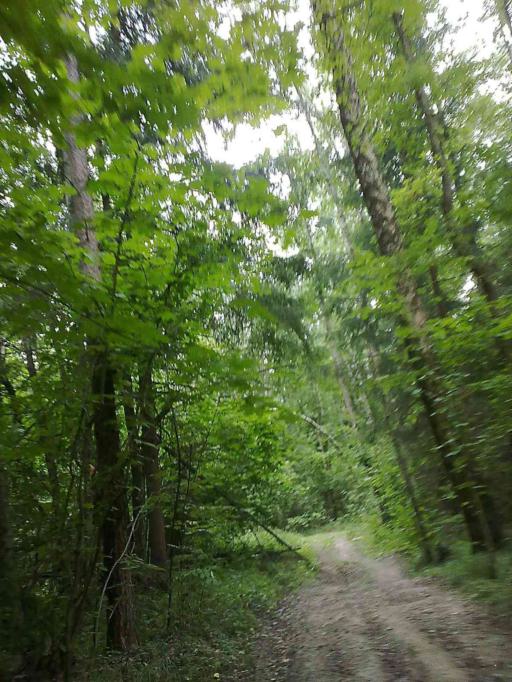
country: RU
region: Moskovskaya
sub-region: Leninskiy Rayon
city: Vnukovo
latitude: 55.6408
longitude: 37.2922
